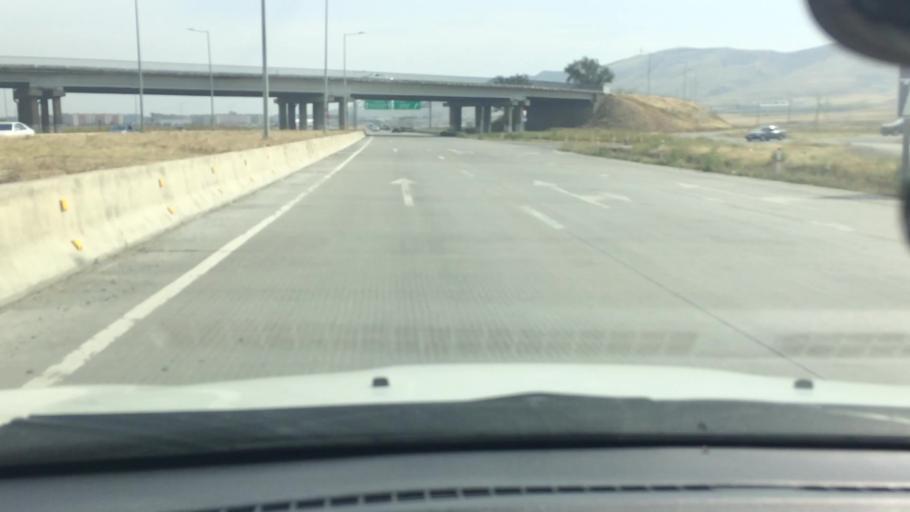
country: GE
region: Kvemo Kartli
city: Rust'avi
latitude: 41.5893
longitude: 44.9478
